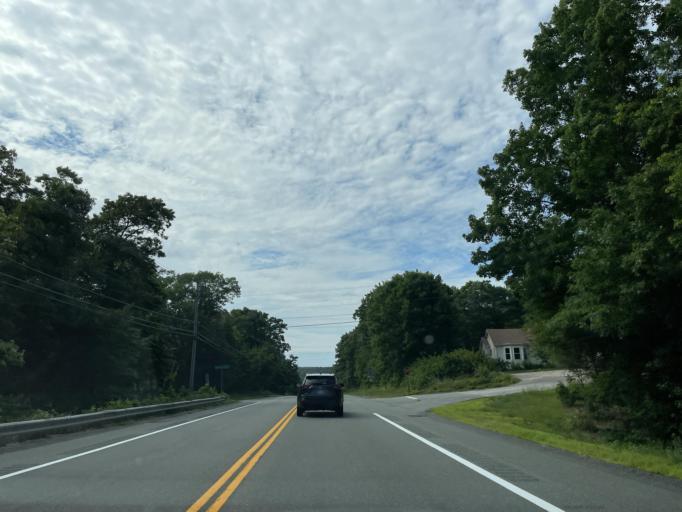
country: US
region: Rhode Island
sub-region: Kent County
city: West Greenwich
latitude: 41.6200
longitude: -71.6738
